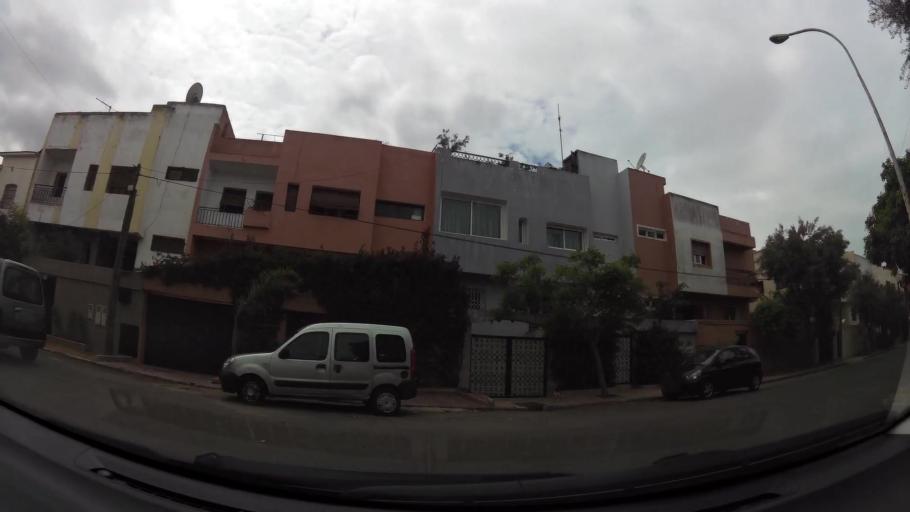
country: MA
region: Grand Casablanca
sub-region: Casablanca
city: Casablanca
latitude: 33.5727
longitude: -7.6648
